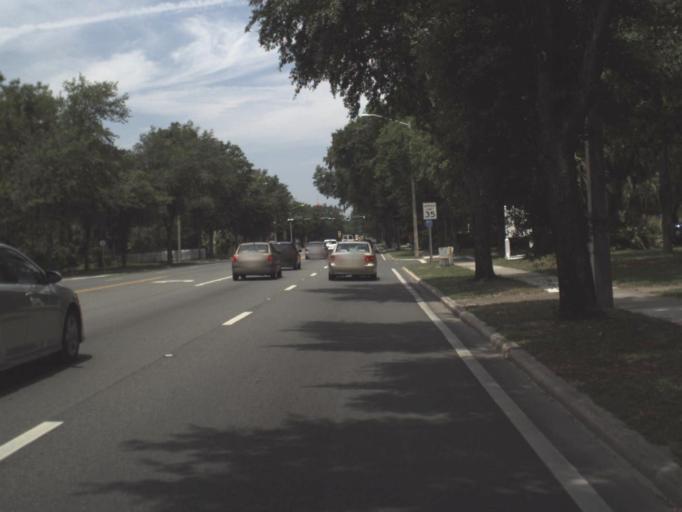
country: US
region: Florida
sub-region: Alachua County
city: Gainesville
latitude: 29.6520
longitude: -82.3156
